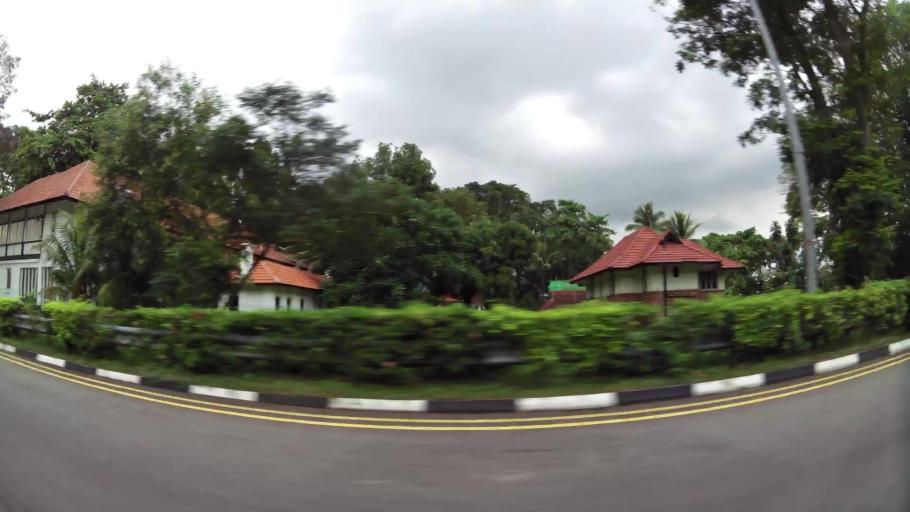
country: MY
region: Johor
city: Kampung Pasir Gudang Baru
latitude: 1.4592
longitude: 103.8282
